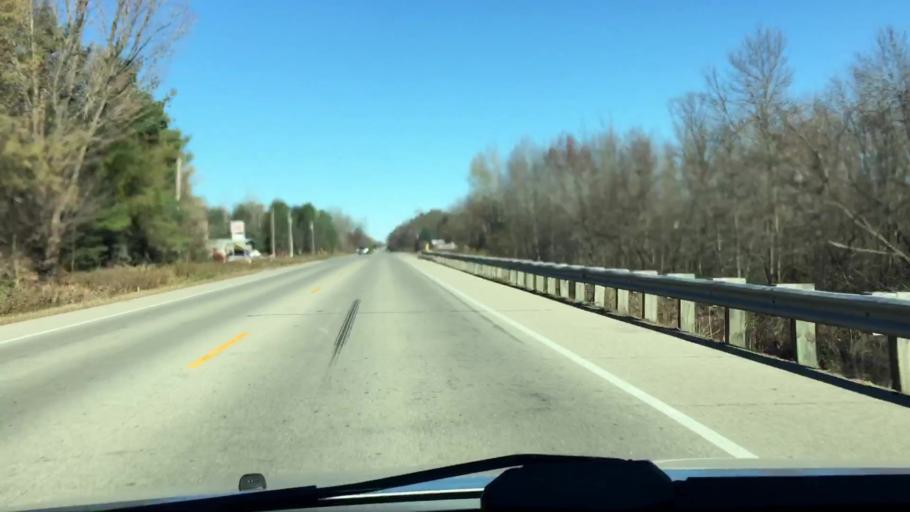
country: US
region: Wisconsin
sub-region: Brown County
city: Pulaski
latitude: 44.7549
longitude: -88.2503
